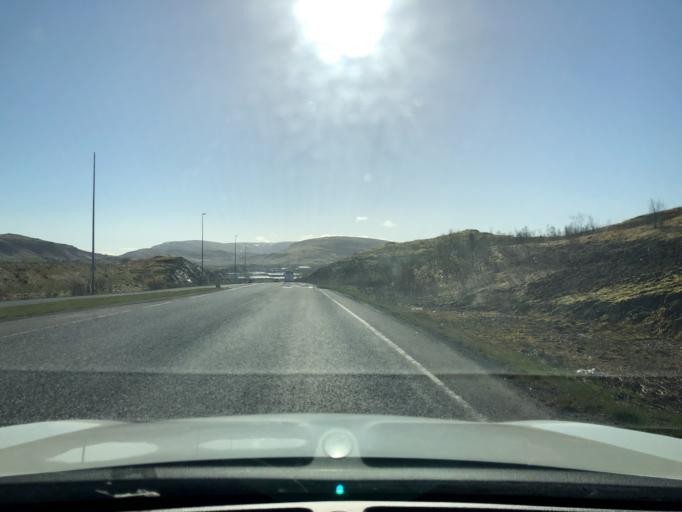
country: IS
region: Capital Region
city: Mosfellsbaer
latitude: 64.1645
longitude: -21.7052
